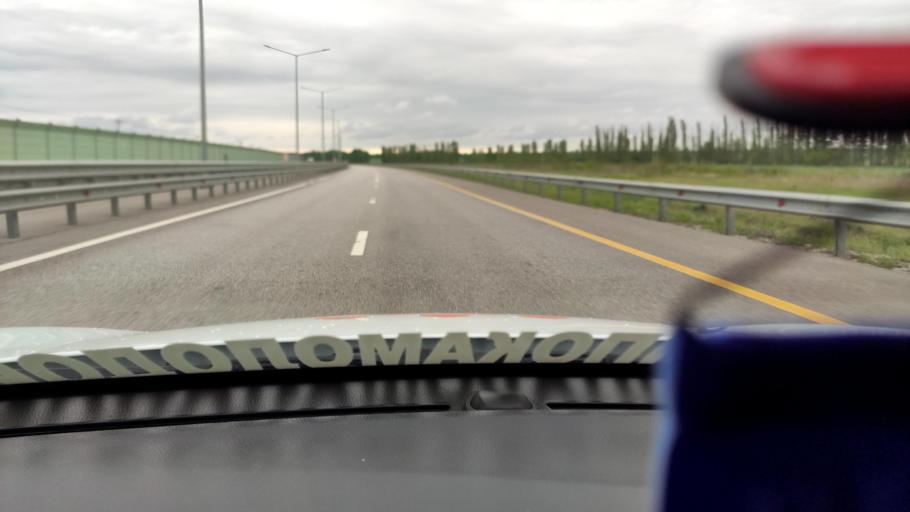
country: RU
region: Voronezj
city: Novaya Usman'
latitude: 51.5900
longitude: 39.3759
